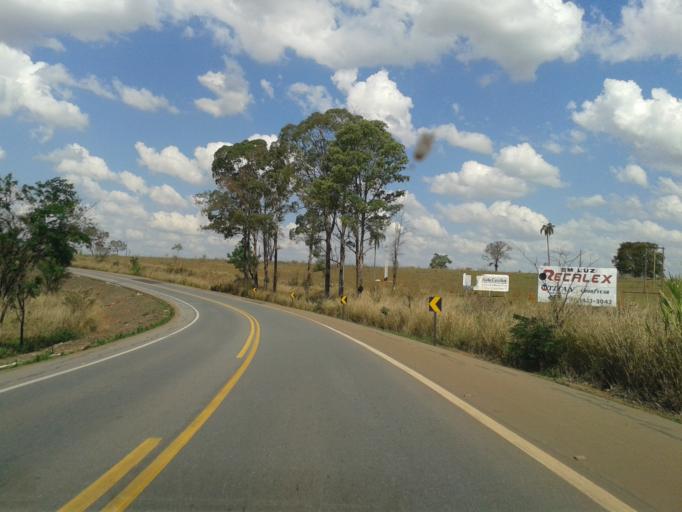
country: BR
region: Minas Gerais
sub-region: Luz
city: Luz
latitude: -19.7724
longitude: -45.7815
